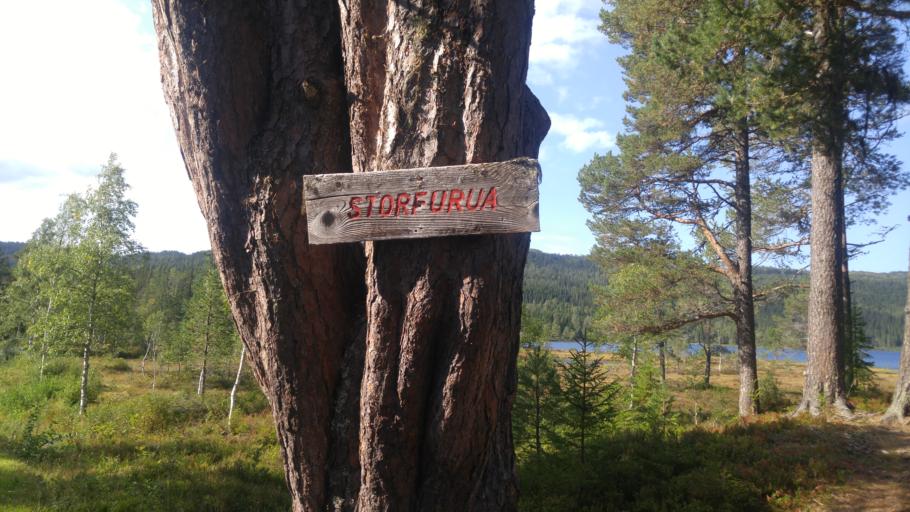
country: NO
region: Sor-Trondelag
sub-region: Melhus
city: Melhus
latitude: 63.3908
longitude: 10.2468
